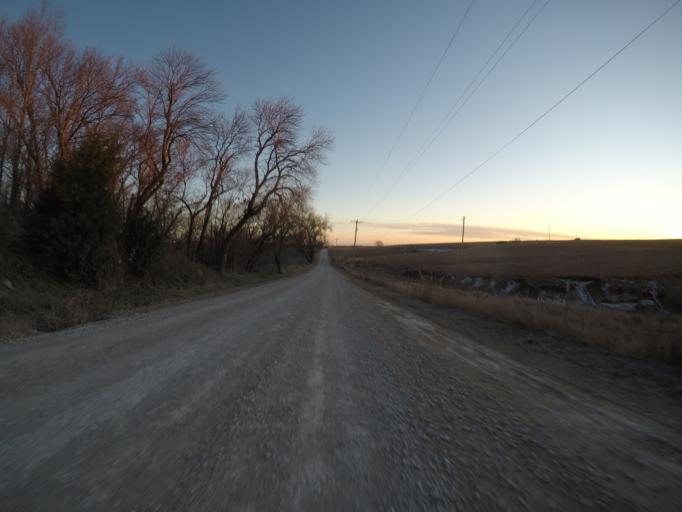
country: US
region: Kansas
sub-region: Riley County
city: Manhattan
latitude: 39.2600
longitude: -96.4827
